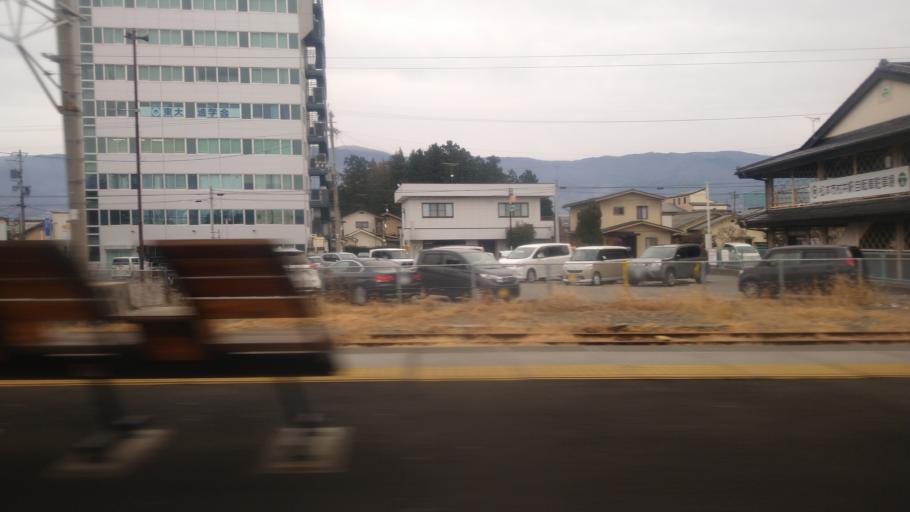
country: JP
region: Nagano
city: Matsumoto
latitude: 36.1747
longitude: 137.9563
